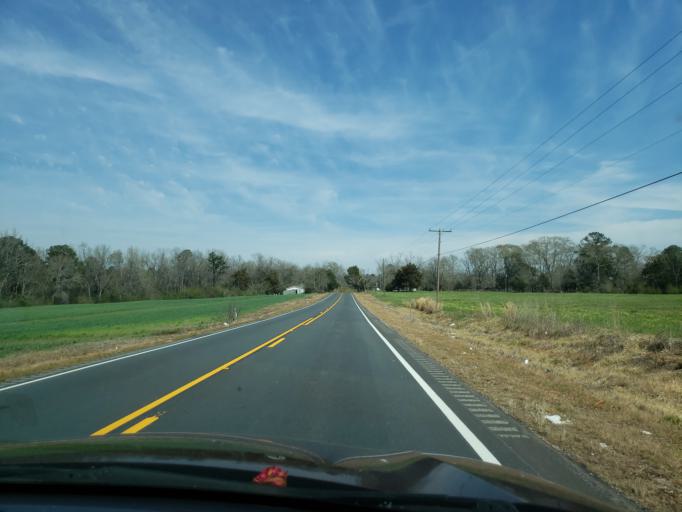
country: US
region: Alabama
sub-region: Elmore County
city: Tallassee
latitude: 32.5612
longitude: -85.7875
